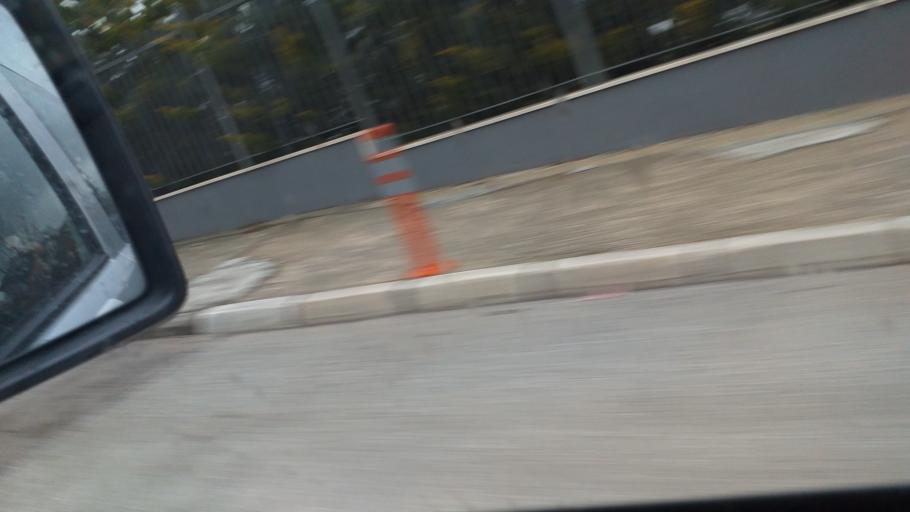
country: TR
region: Ankara
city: Batikent
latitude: 39.8759
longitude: 32.7158
